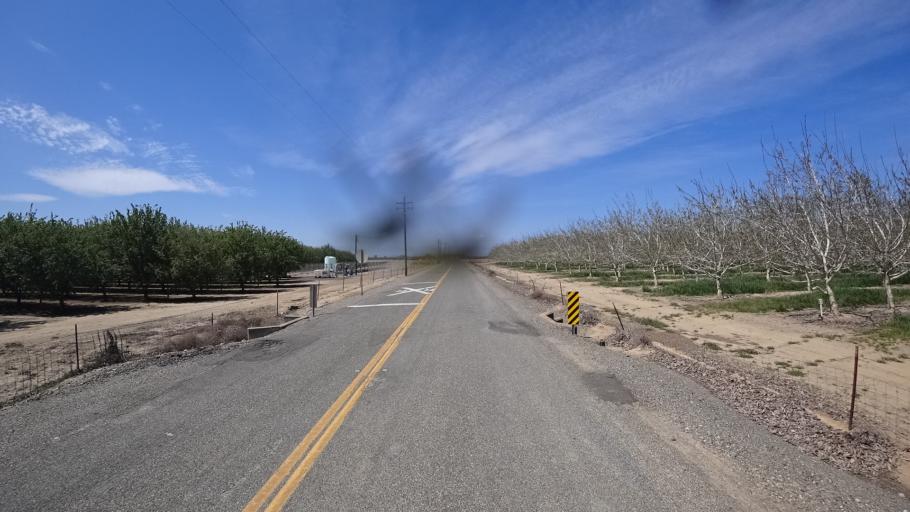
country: US
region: California
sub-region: Glenn County
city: Orland
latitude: 39.6533
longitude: -122.1950
